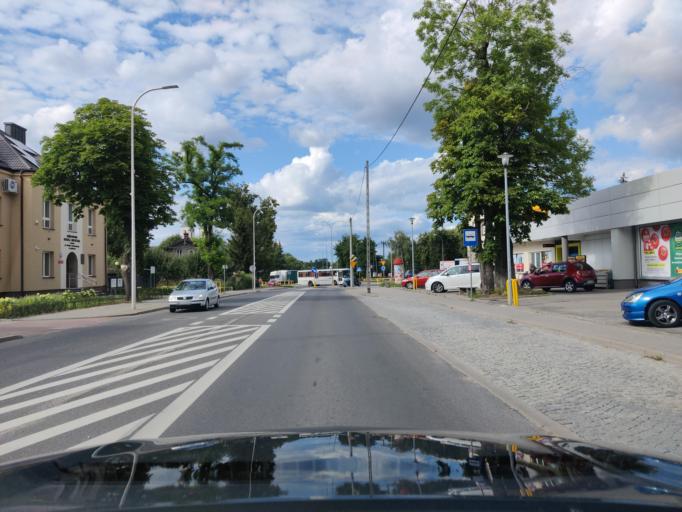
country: PL
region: Podlasie
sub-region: Powiat zambrowski
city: Zambrow
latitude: 52.9792
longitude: 22.2451
